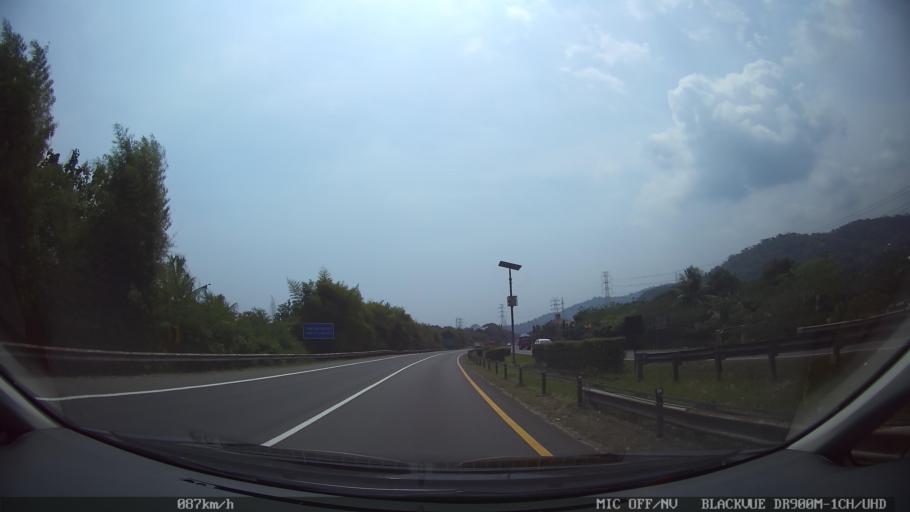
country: ID
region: Banten
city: Curug
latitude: -5.9899
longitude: 106.0411
